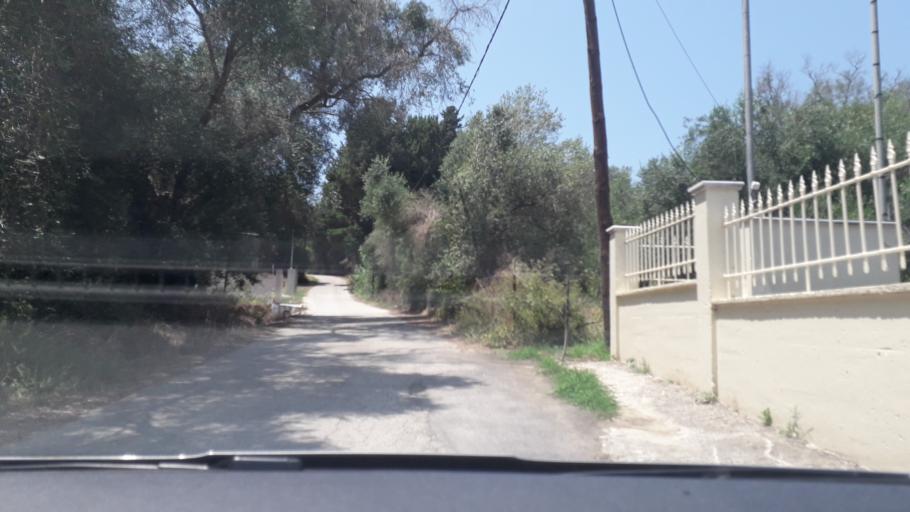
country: GR
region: Ionian Islands
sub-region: Nomos Kerkyras
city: Lefkimmi
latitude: 39.3798
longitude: 20.1104
